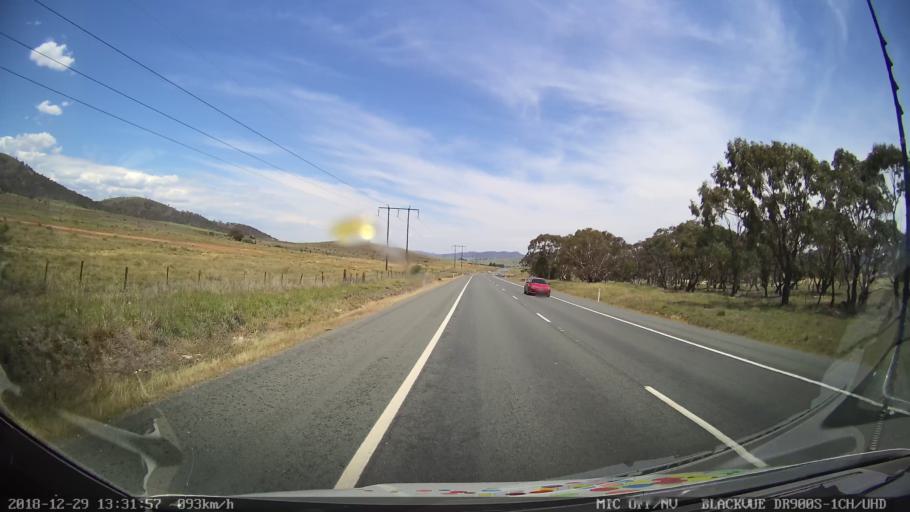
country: AU
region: New South Wales
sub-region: Cooma-Monaro
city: Cooma
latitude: -35.9239
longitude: 149.1518
